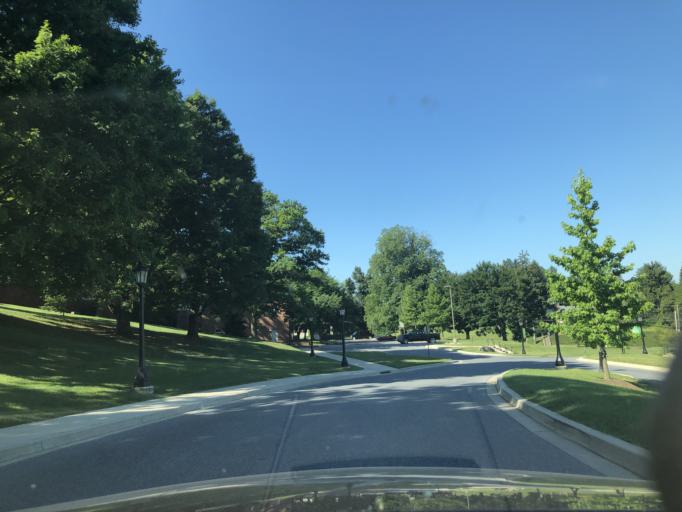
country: US
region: Maryland
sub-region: Carroll County
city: Westminster
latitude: 39.5842
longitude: -77.0026
